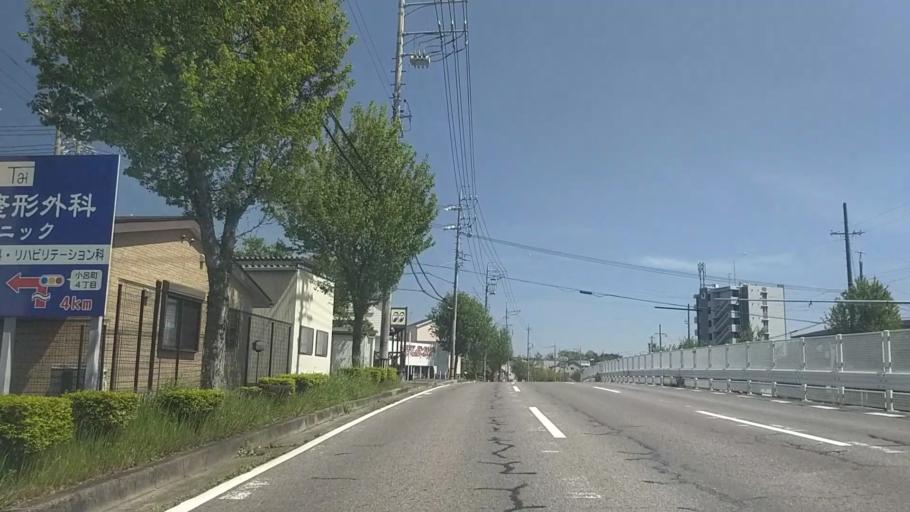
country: JP
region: Aichi
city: Okazaki
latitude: 34.9776
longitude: 137.1753
